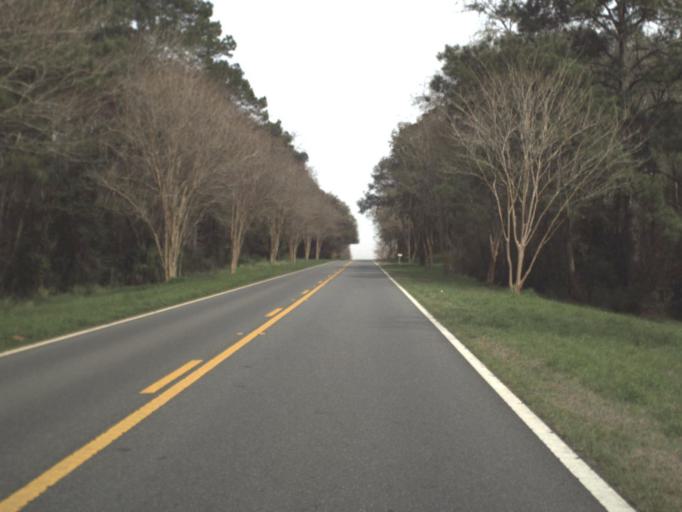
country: US
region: Florida
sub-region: Jefferson County
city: Monticello
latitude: 30.5262
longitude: -84.0089
